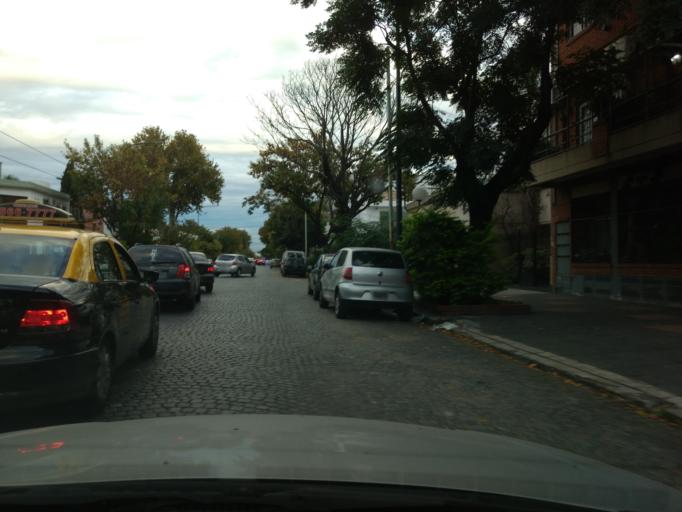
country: AR
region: Buenos Aires F.D.
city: Villa Santa Rita
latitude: -34.6316
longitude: -58.4929
